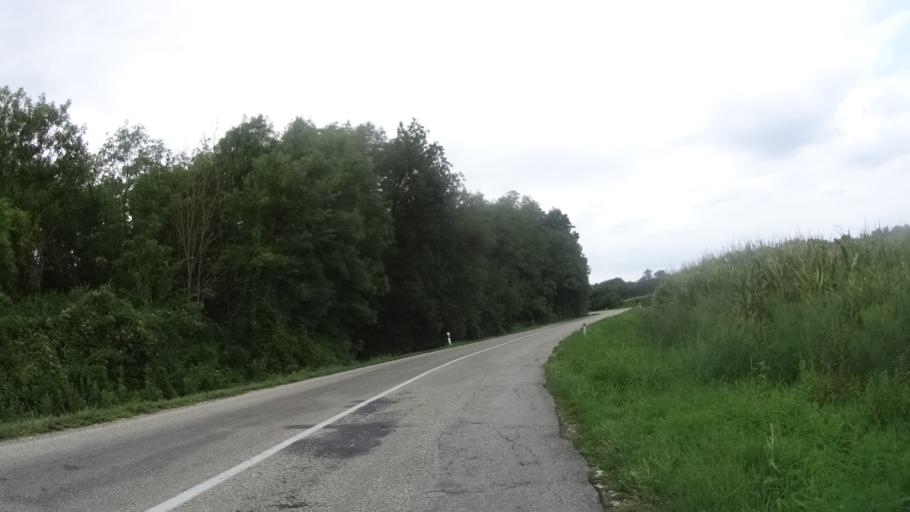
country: SK
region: Trnavsky
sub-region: Okres Dunajska Streda
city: Velky Meder
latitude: 47.7539
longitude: 17.7980
